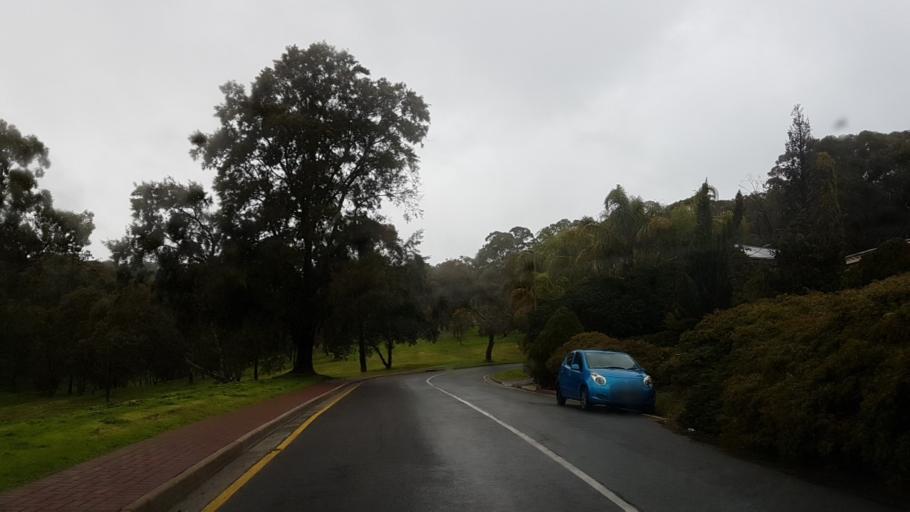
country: AU
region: South Australia
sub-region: Onkaparinga
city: Craigburn Farm
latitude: -35.0836
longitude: 138.5952
